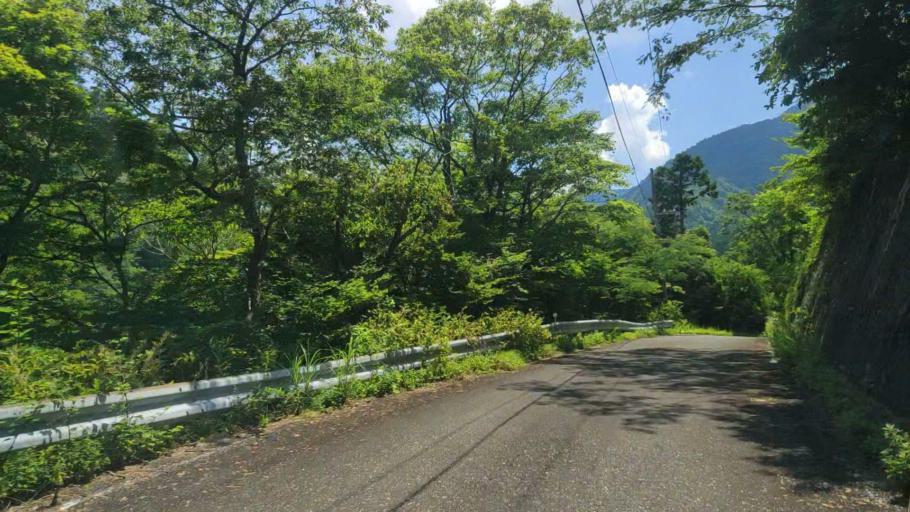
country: JP
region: Fukui
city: Ono
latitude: 35.7396
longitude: 136.5829
